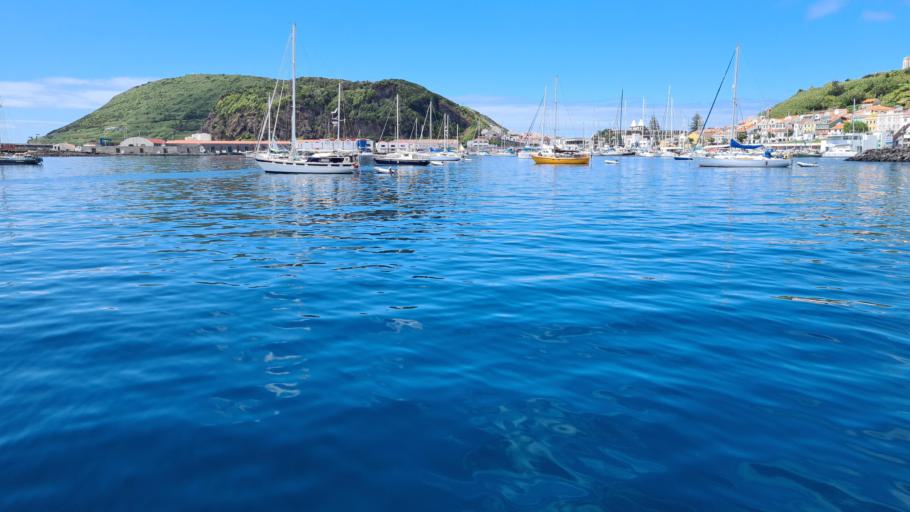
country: PT
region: Azores
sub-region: Horta
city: Horta
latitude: 38.5326
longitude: -28.6231
